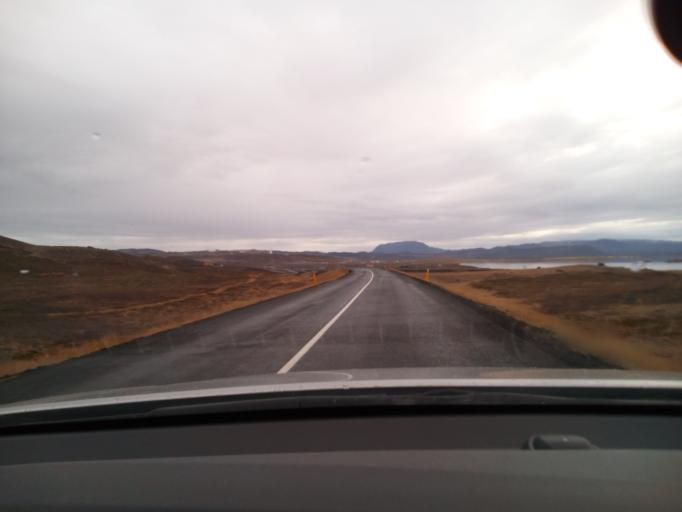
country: IS
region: Northeast
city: Laugar
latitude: 65.6616
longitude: -16.9790
